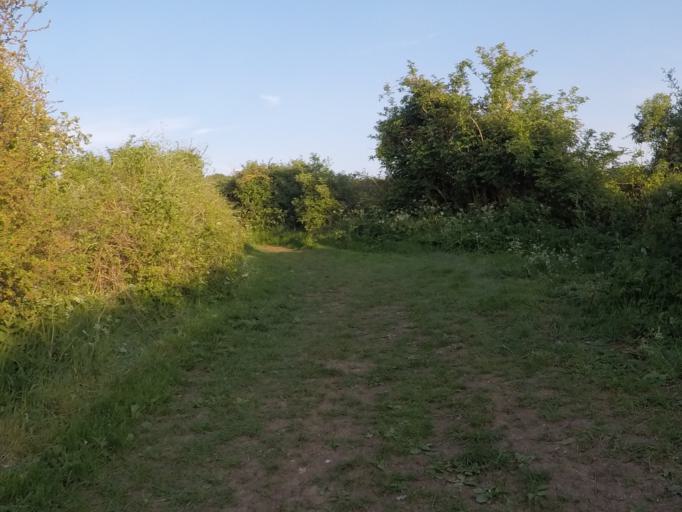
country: GB
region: England
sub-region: Oxfordshire
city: Charlbury
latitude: 51.8678
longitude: -1.5356
